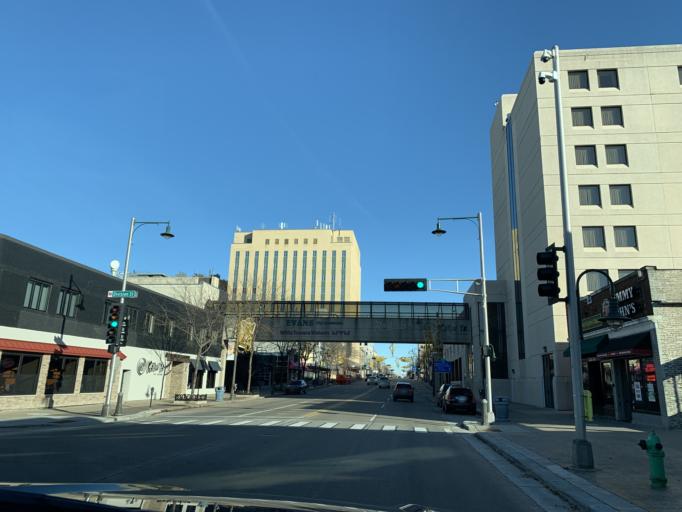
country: US
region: Wisconsin
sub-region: Outagamie County
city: Appleton
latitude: 44.2617
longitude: -88.4109
